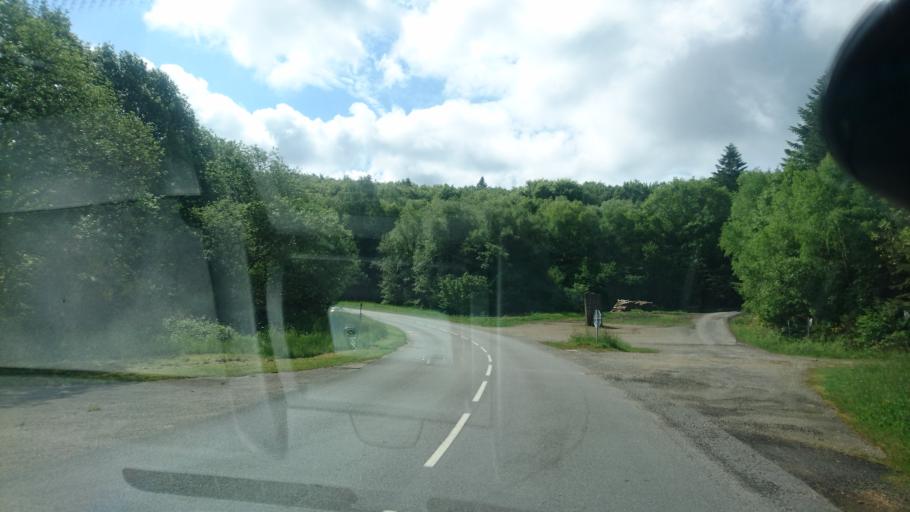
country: FR
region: Limousin
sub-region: Departement de la Haute-Vienne
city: Peyrat-le-Chateau
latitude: 45.7965
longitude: 1.8417
